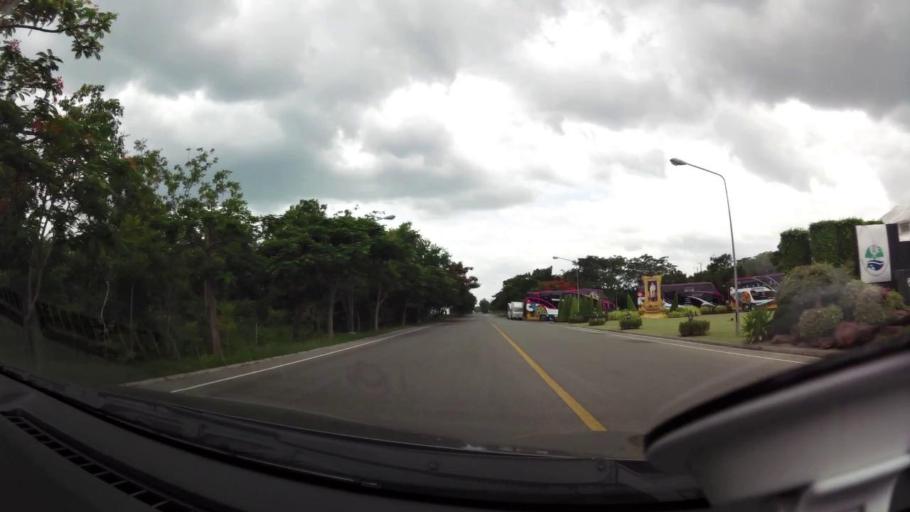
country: TH
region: Phetchaburi
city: Cha-am
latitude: 12.7035
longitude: 99.9585
